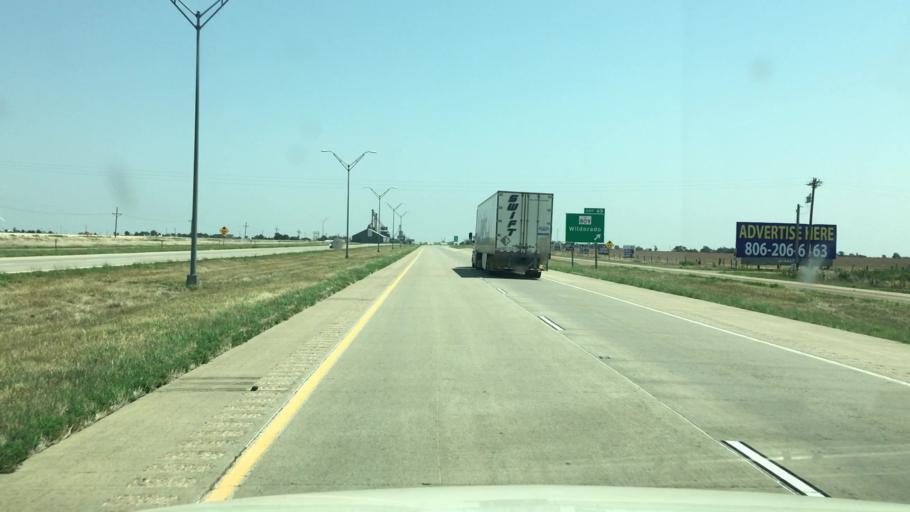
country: US
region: Texas
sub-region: Potter County
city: Bushland
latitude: 35.2098
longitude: -102.2213
